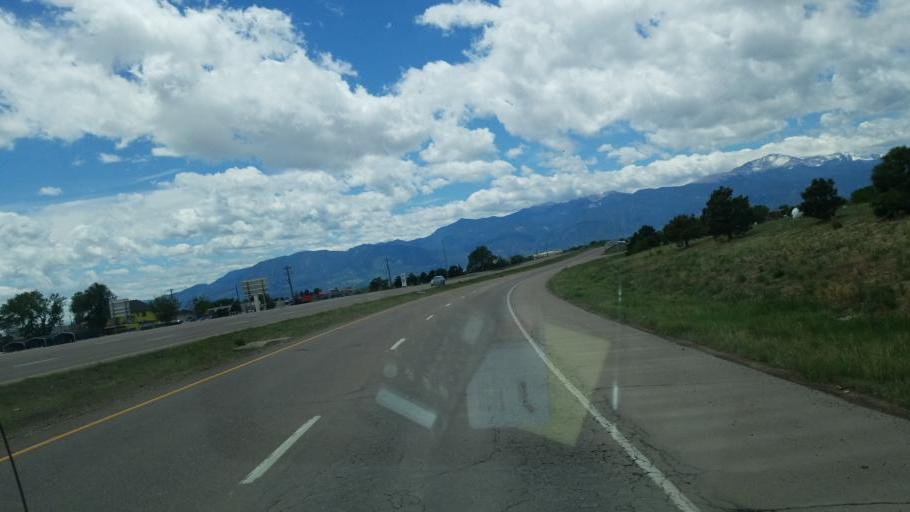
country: US
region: Colorado
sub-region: El Paso County
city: Cimarron Hills
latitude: 38.8405
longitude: -104.6961
